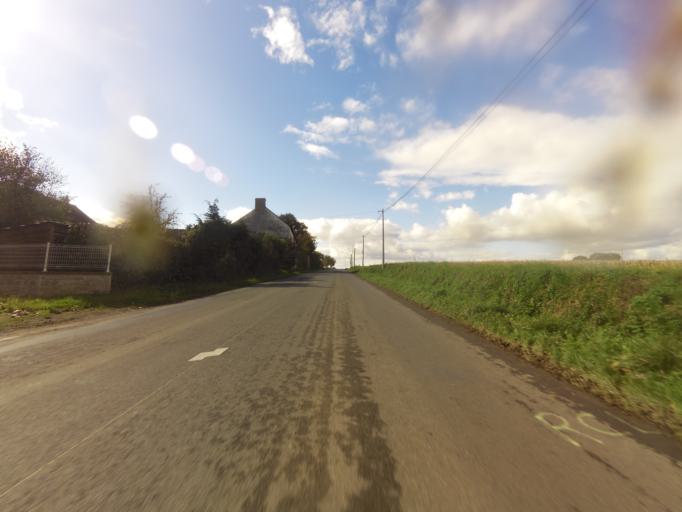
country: FR
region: Brittany
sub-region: Departement d'Ille-et-Vilaine
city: Erce-pres-Liffre
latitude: 48.2555
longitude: -1.5373
